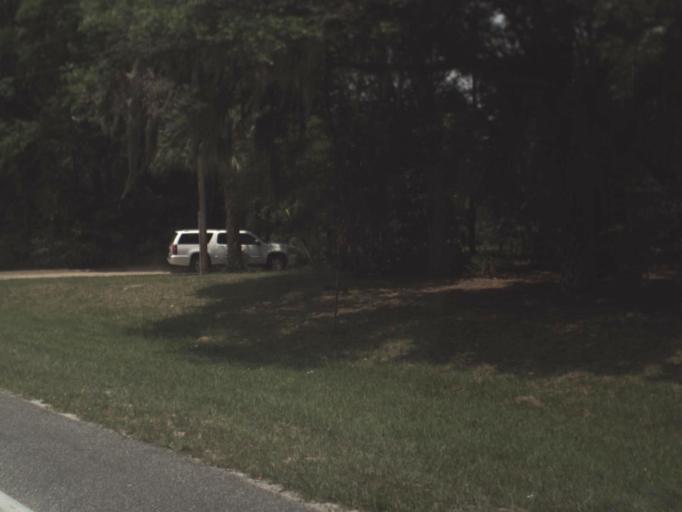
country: US
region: Florida
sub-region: Putnam County
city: Palatka
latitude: 29.6223
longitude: -81.6992
